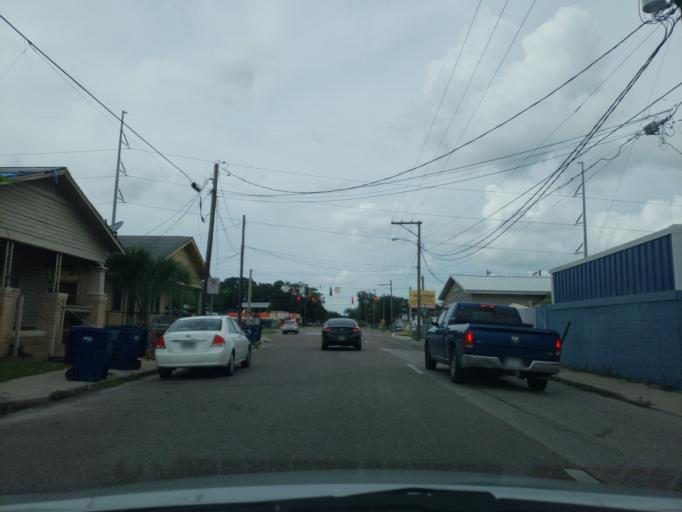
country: US
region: Florida
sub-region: Hillsborough County
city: Tampa
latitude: 27.9770
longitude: -82.4429
